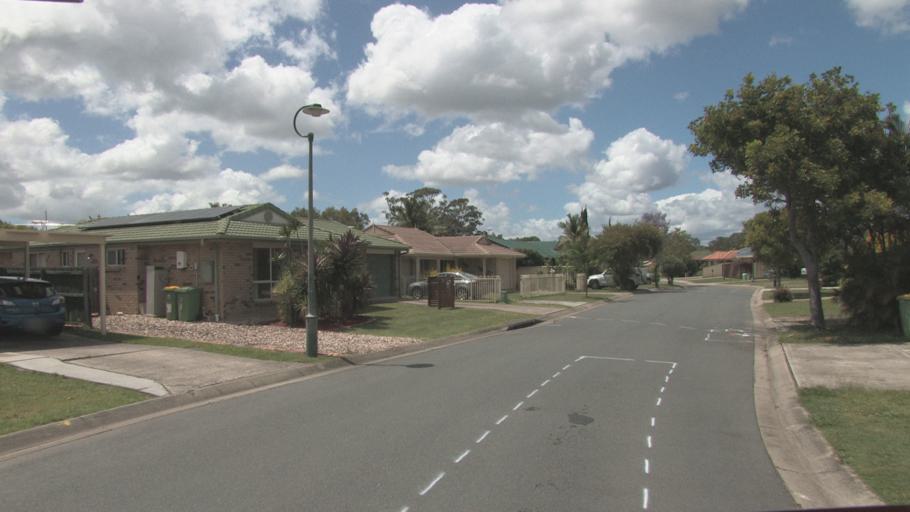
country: AU
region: Queensland
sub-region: Logan
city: Beenleigh
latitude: -27.6958
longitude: 153.1838
